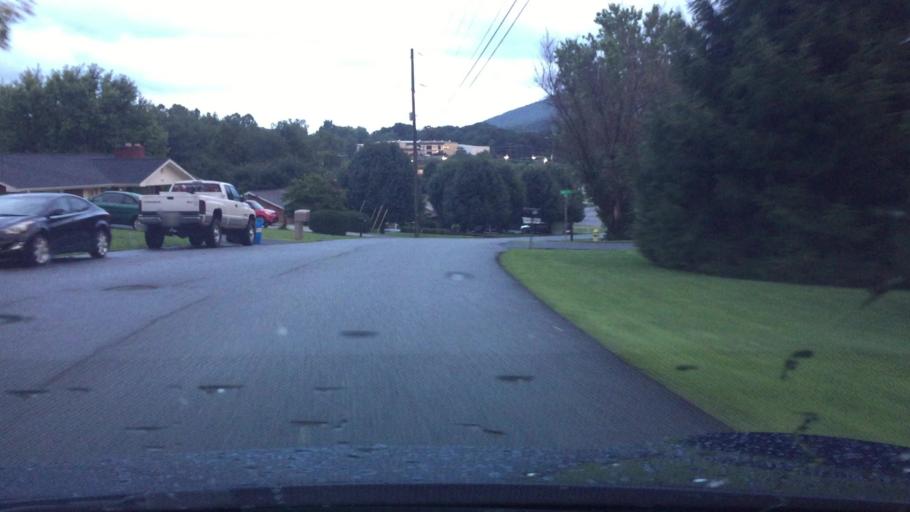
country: US
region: Virginia
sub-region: Pulaski County
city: Pulaski
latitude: 37.0553
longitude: -80.7515
